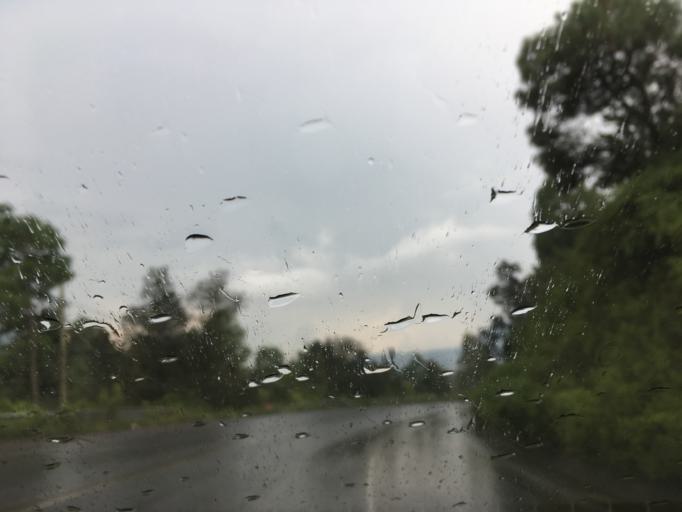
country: MX
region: Michoacan
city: Angahuan
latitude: 19.5561
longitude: -102.2214
